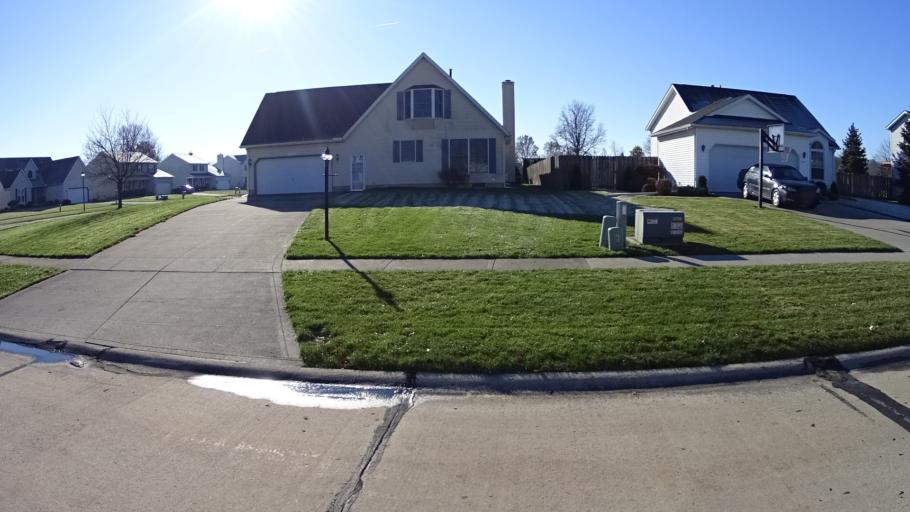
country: US
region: Ohio
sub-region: Lorain County
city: North Ridgeville
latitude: 41.4146
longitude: -82.0083
